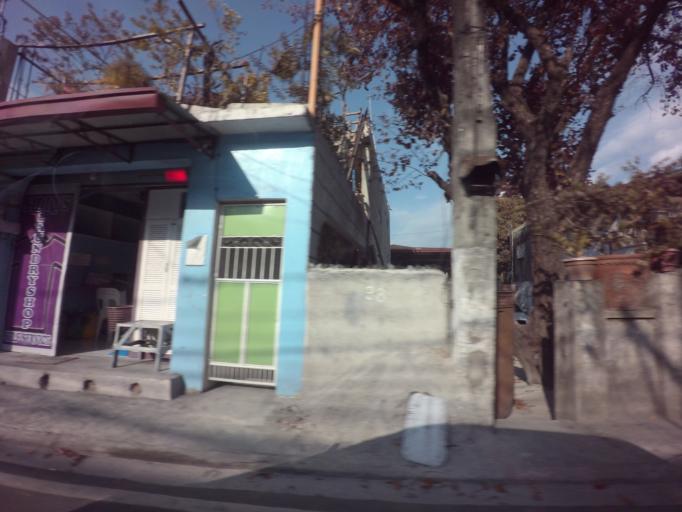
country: PH
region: Calabarzon
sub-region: Province of Rizal
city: Taguig
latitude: 14.4829
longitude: 121.0612
